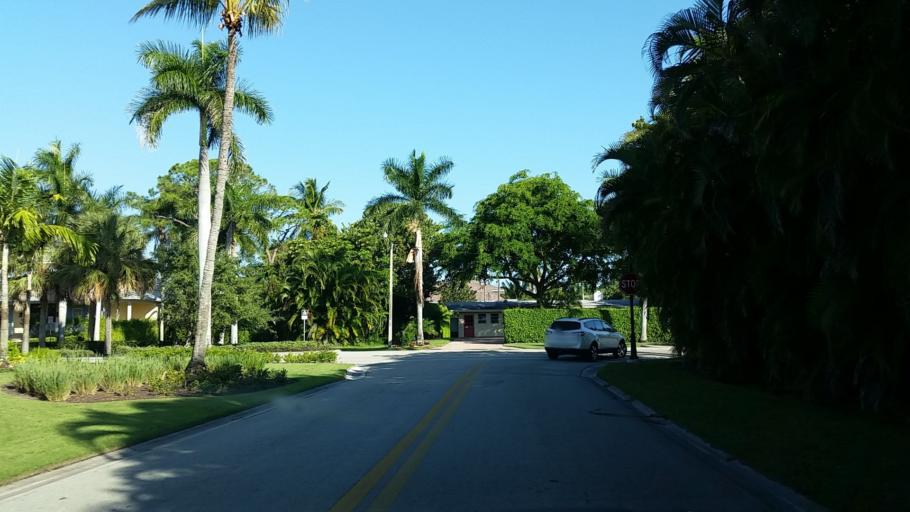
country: US
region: Florida
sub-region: Collier County
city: Naples
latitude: 26.1458
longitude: -81.8052
